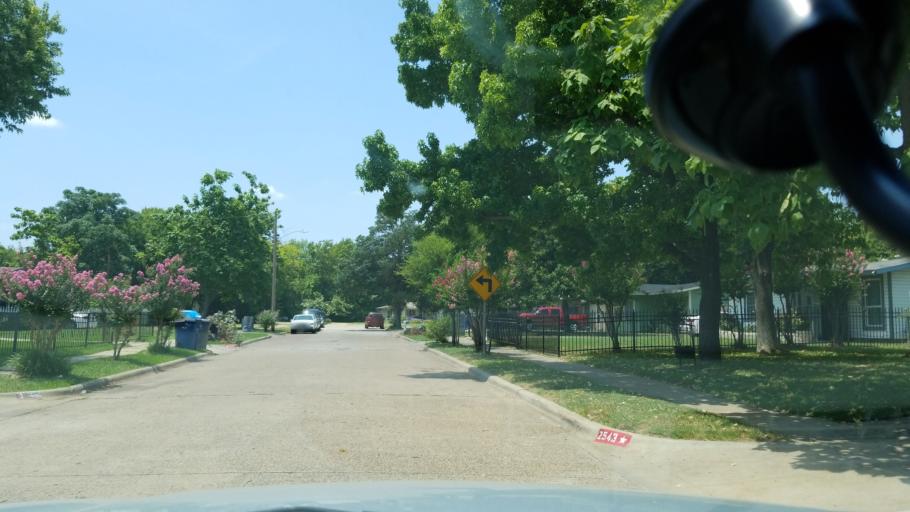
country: US
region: Texas
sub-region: Dallas County
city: Cockrell Hill
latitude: 32.7231
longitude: -96.8605
